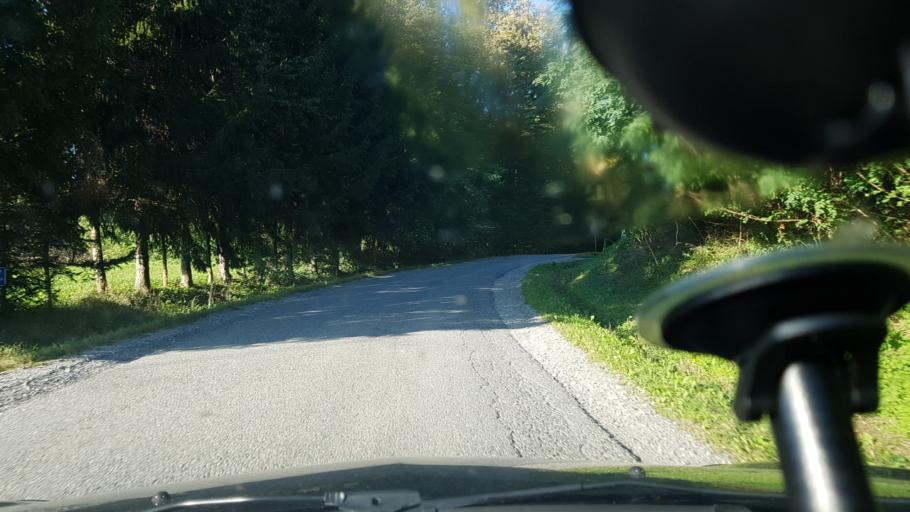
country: HR
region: Bjelovarsko-Bilogorska
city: Bjelovar
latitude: 45.9276
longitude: 16.8648
